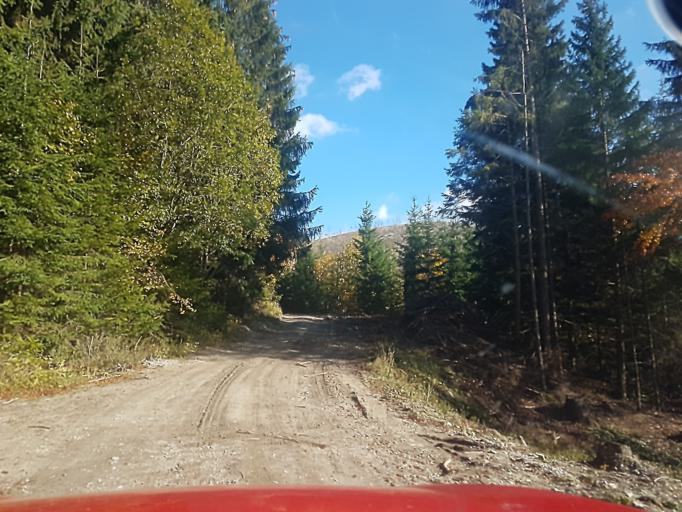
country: SK
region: Zilinsky
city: Ruzomberok
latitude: 49.1332
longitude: 19.3573
